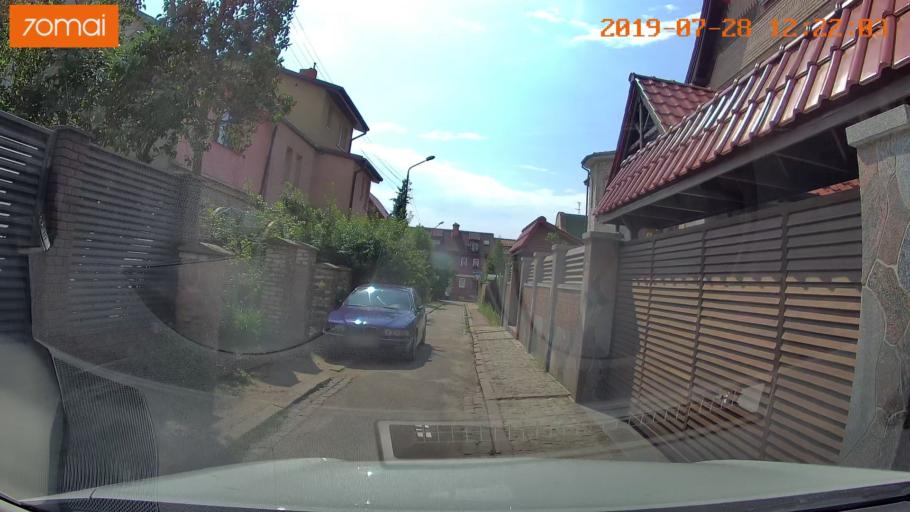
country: RU
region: Kaliningrad
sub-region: Gorod Kaliningrad
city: Kaliningrad
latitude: 54.7120
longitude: 20.4557
